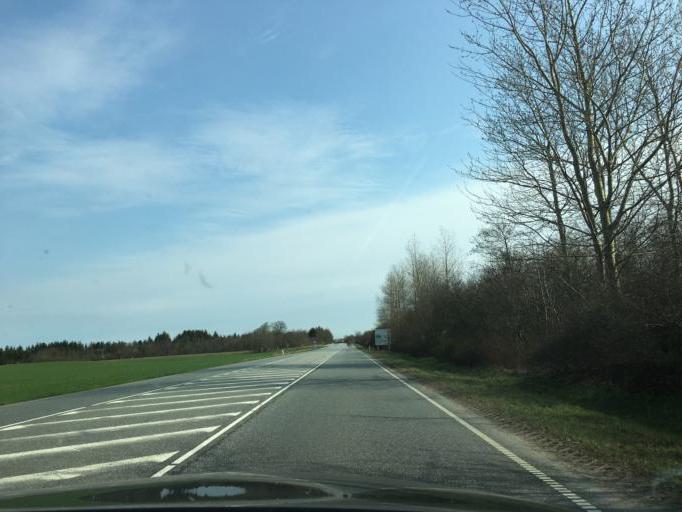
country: DK
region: South Denmark
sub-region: Kolding Kommune
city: Lunderskov
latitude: 55.4905
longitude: 9.2935
